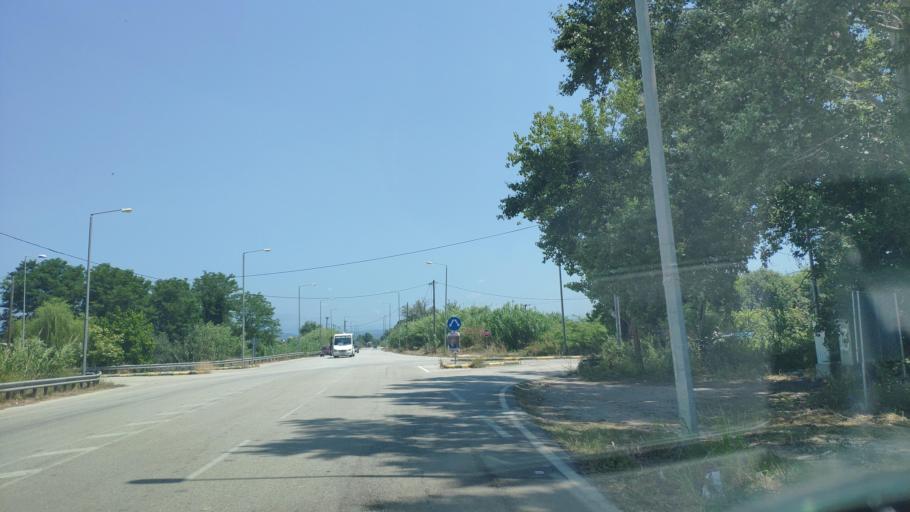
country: GR
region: Epirus
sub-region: Nomos Artas
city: Aneza
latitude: 39.1006
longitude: 20.9128
